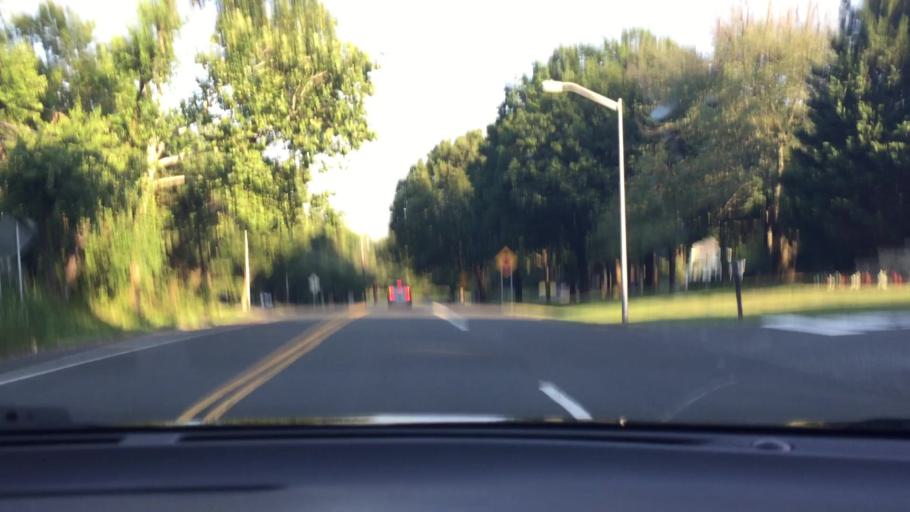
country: US
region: Maryland
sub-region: Montgomery County
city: Potomac
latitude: 39.0221
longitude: -77.1823
